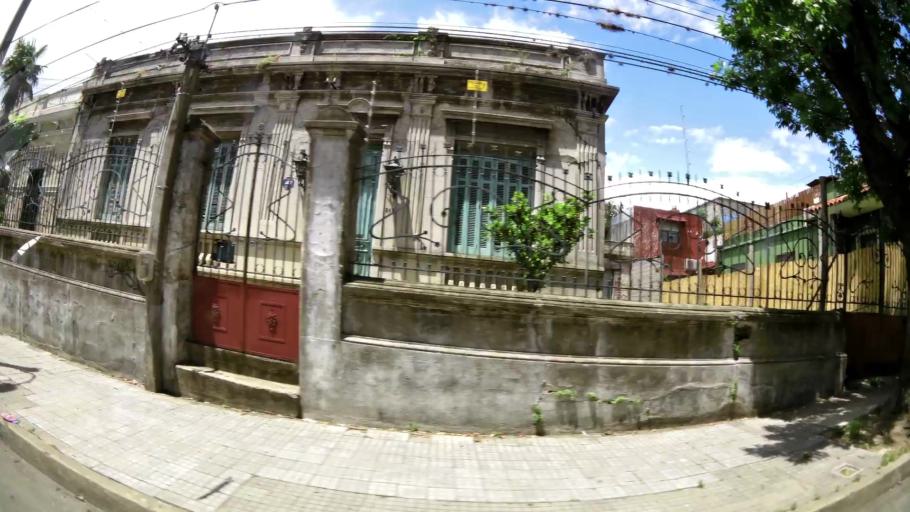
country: UY
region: Montevideo
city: Montevideo
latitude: -34.8604
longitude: -56.1858
